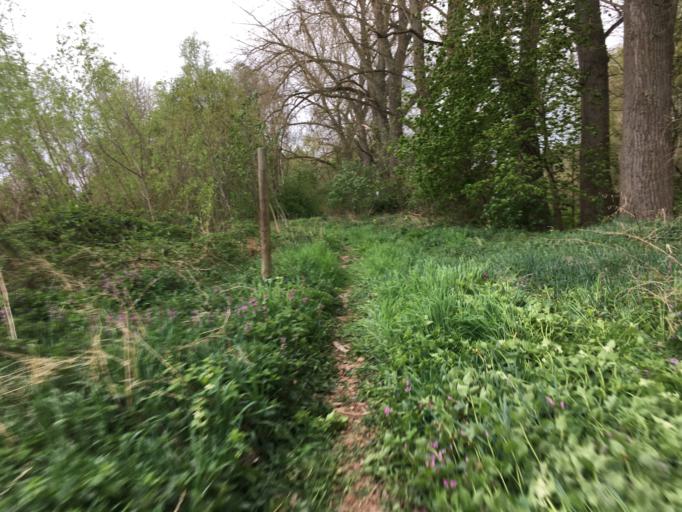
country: DE
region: Baden-Wuerttemberg
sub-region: Regierungsbezirk Stuttgart
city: Nordheim
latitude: 49.1049
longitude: 9.1497
